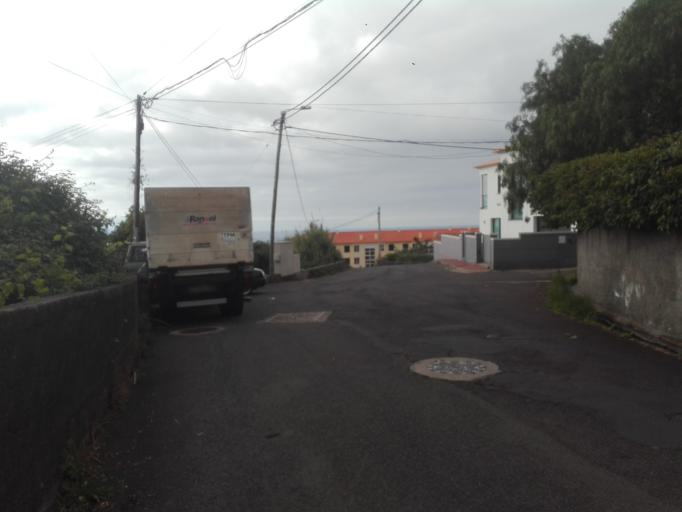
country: PT
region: Madeira
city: Canico
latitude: 32.6540
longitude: -16.8288
